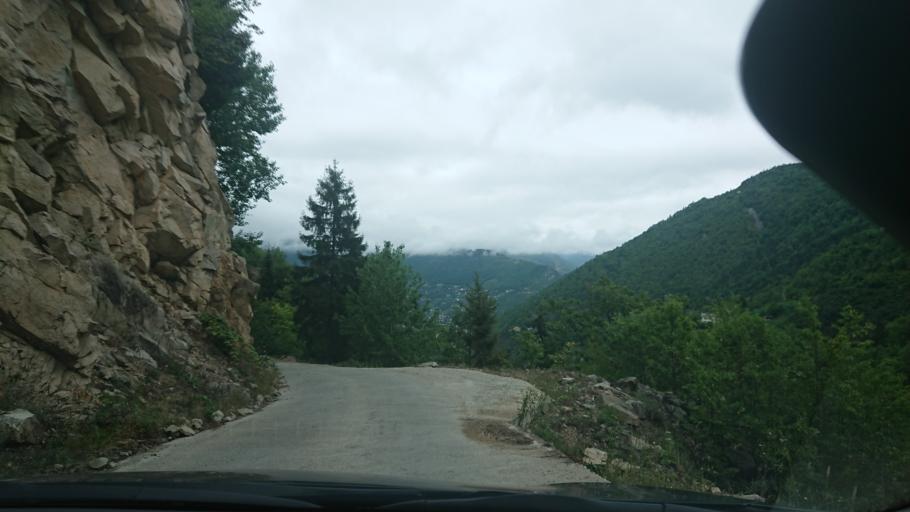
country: TR
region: Gumushane
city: Kurtun
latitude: 40.6833
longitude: 39.0500
